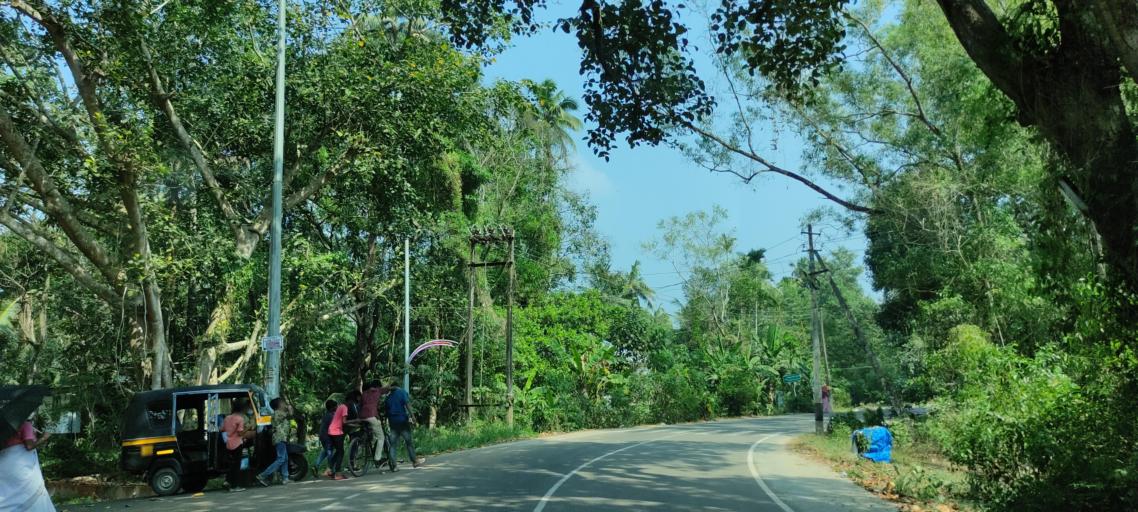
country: IN
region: Kerala
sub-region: Alappuzha
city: Shertallai
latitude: 9.6016
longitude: 76.3177
